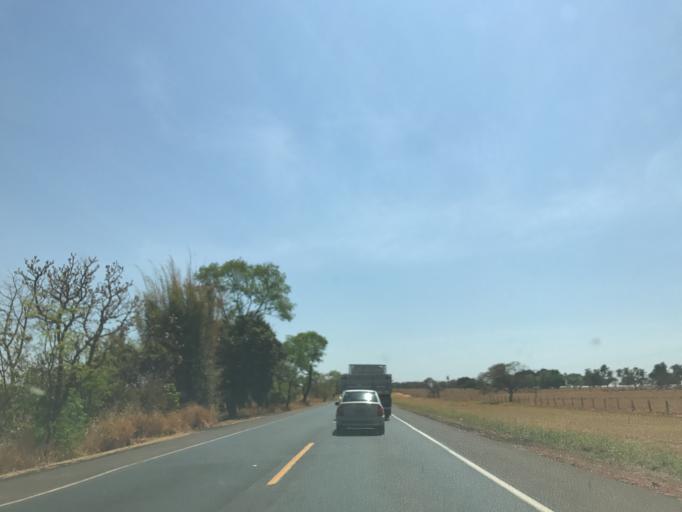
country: BR
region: Minas Gerais
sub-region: Frutal
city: Frutal
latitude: -20.0417
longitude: -49.0502
